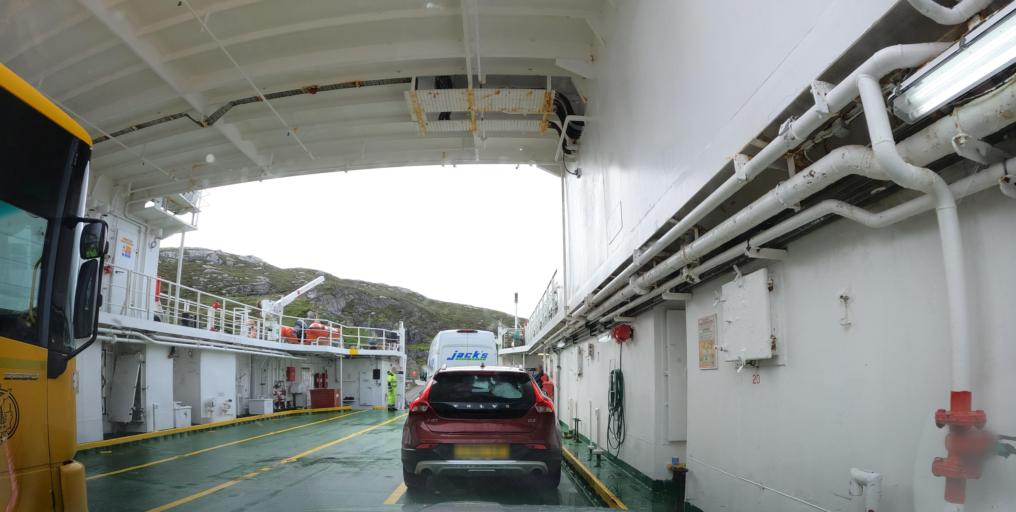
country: GB
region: Scotland
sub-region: Eilean Siar
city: Barra
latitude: 57.0711
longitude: -7.3083
